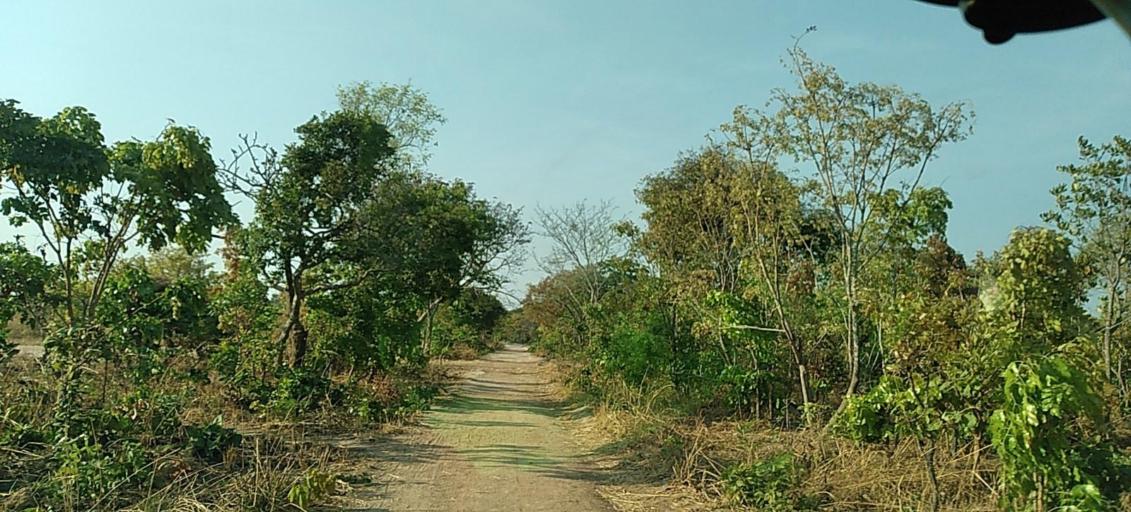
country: ZM
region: North-Western
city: Kalengwa
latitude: -13.1575
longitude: 25.0341
